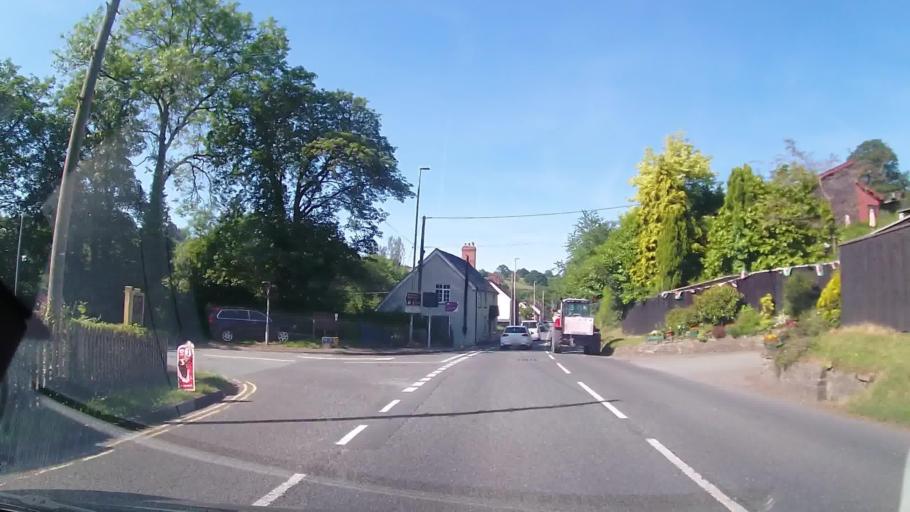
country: GB
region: Wales
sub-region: Sir Powys
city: Llanfyllin
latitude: 52.6517
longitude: -3.3229
